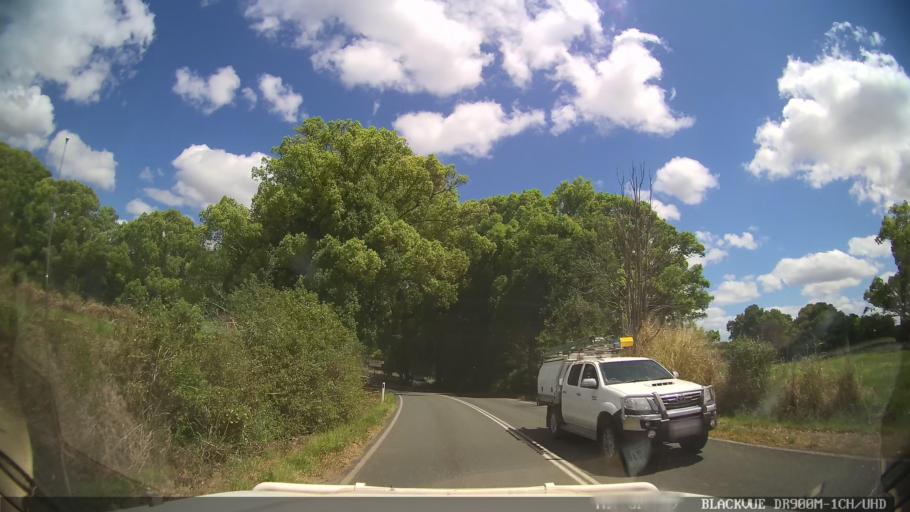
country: AU
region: Queensland
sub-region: Sunshine Coast
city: Nambour
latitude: -26.6479
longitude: 152.8150
